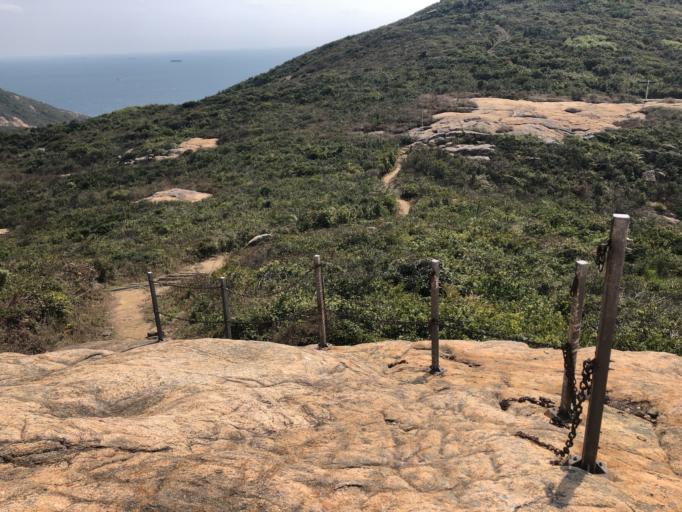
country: HK
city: Sok Kwu Wan
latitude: 22.1679
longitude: 114.2608
